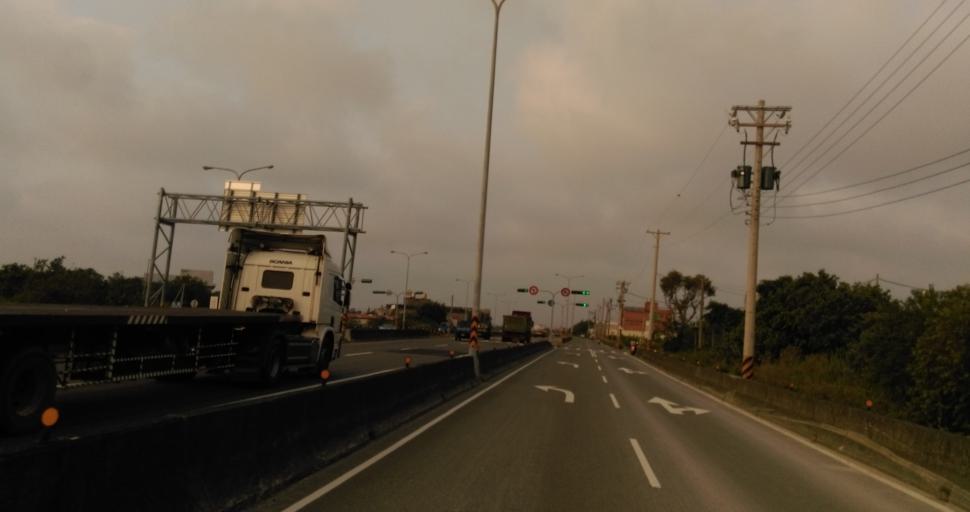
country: TW
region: Taiwan
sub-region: Hsinchu
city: Hsinchu
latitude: 24.7847
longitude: 120.9163
